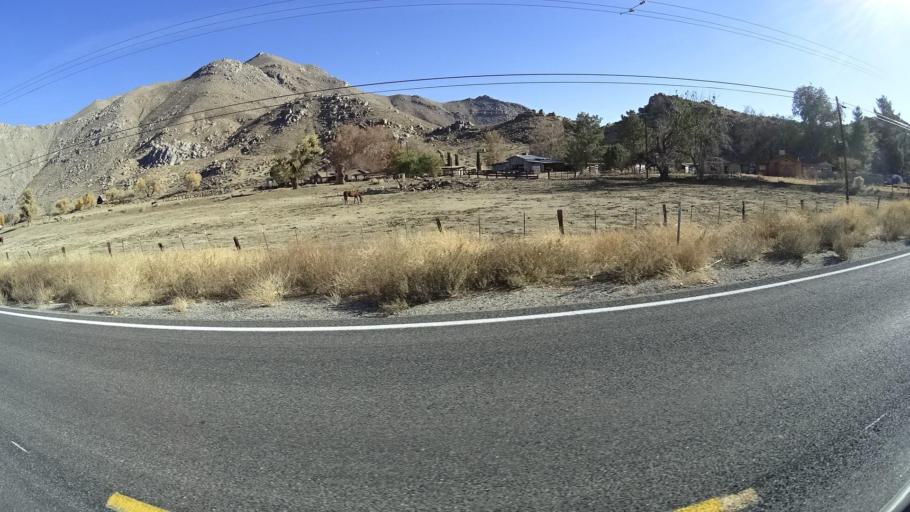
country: US
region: California
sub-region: Kern County
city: Weldon
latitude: 35.6715
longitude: -118.2615
